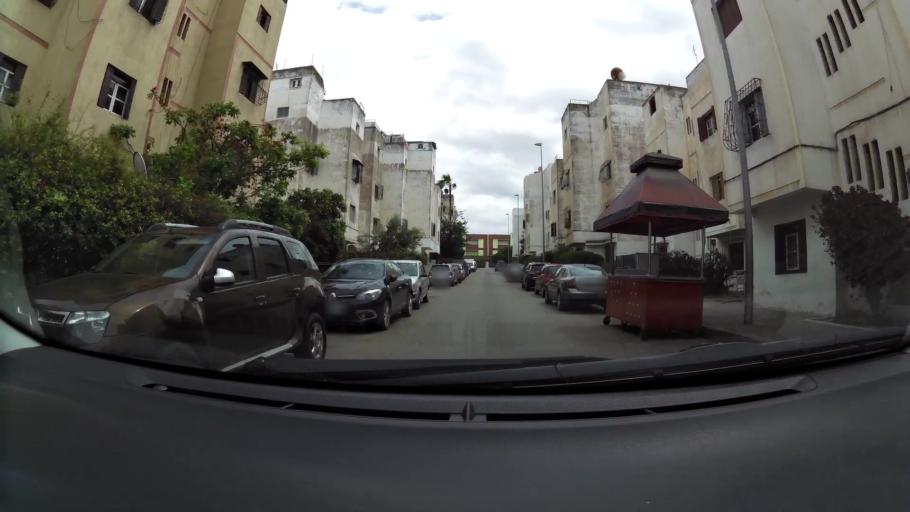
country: MA
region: Grand Casablanca
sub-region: Casablanca
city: Casablanca
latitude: 33.5785
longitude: -7.5612
